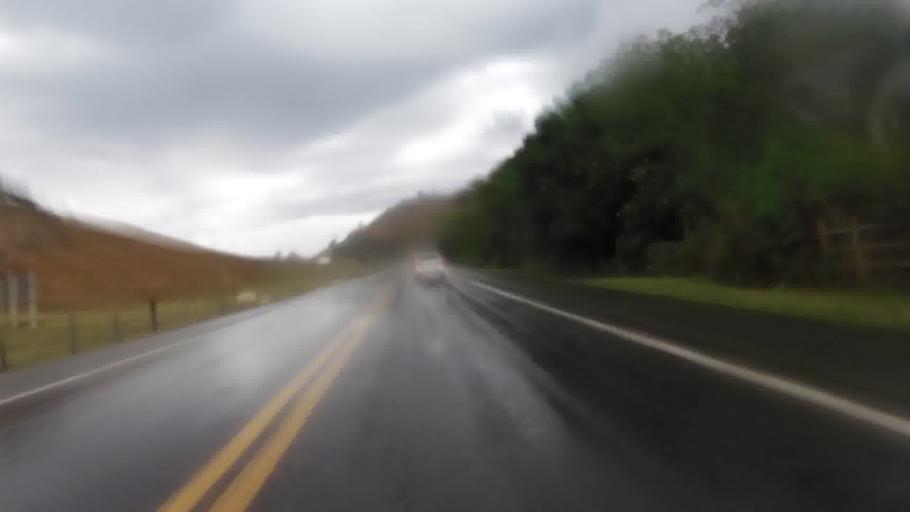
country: BR
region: Espirito Santo
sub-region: Cachoeiro De Itapemirim
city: Cachoeiro de Itapemirim
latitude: -20.9634
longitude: -41.1047
